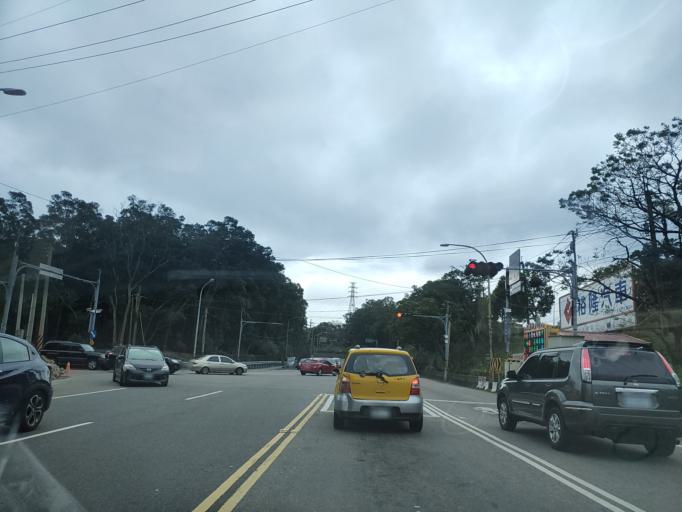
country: TW
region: Taiwan
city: Fengyuan
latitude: 24.3938
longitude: 120.7573
